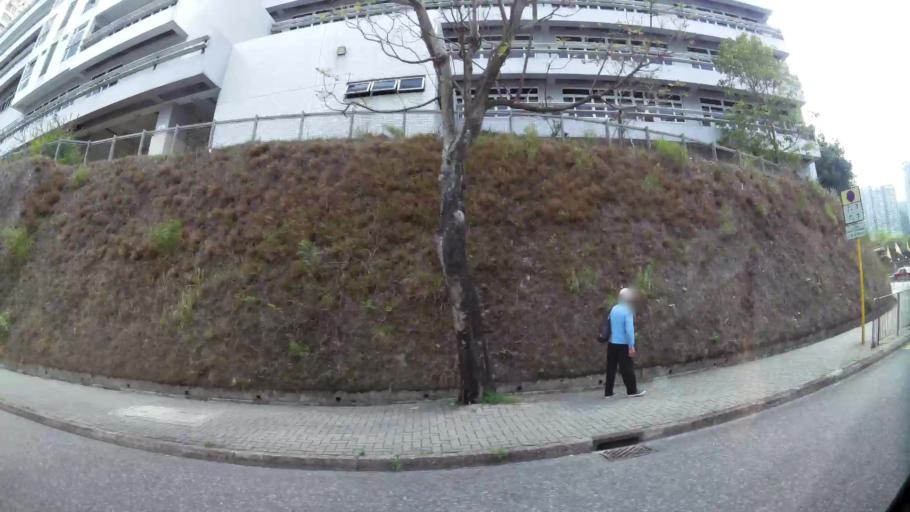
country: HK
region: Kowloon City
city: Kowloon
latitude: 22.3146
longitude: 114.2340
